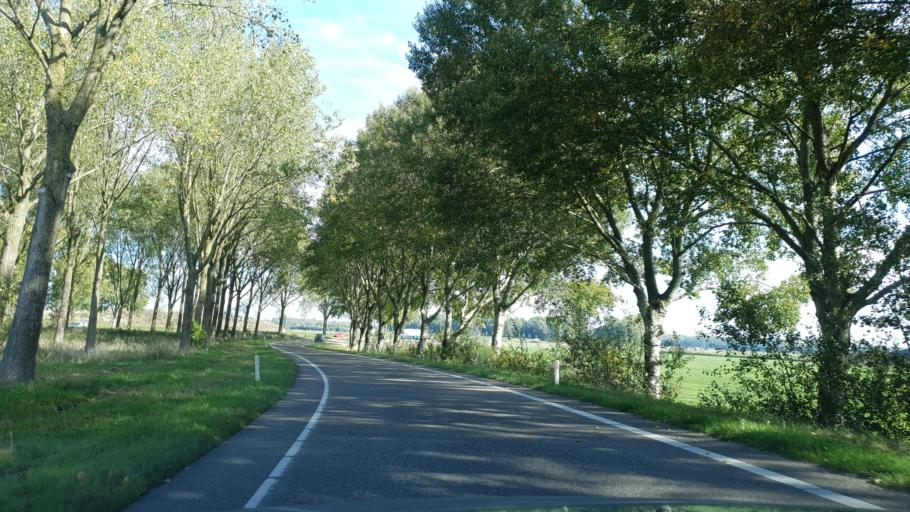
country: NL
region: Gelderland
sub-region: Gemeente Wijchen
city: Bergharen
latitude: 51.8706
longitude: 5.6622
